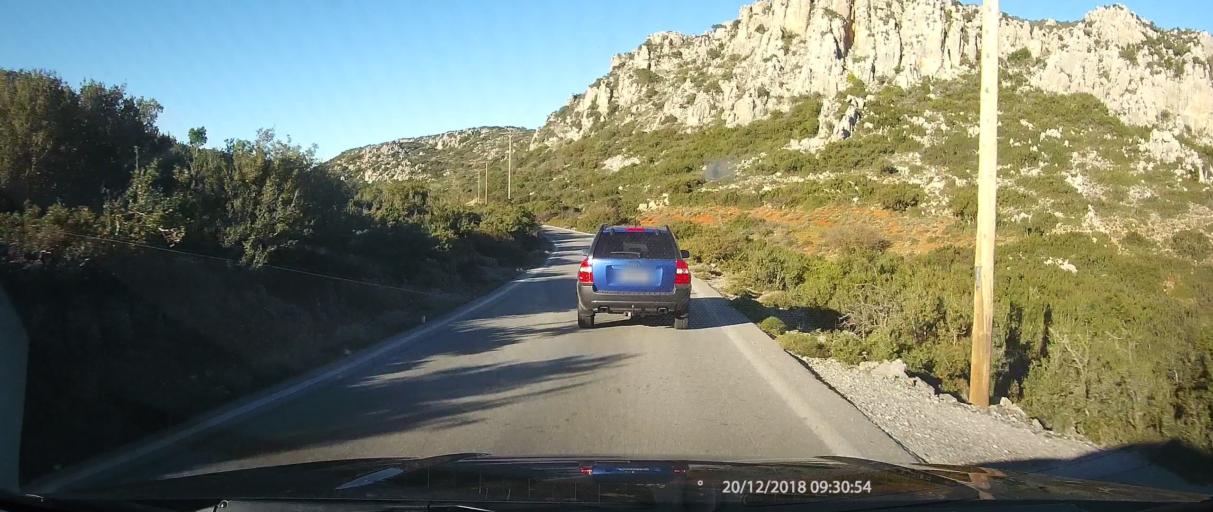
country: GR
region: Peloponnese
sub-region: Nomos Lakonias
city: Kato Glikovrisi
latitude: 36.9525
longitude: 22.8405
